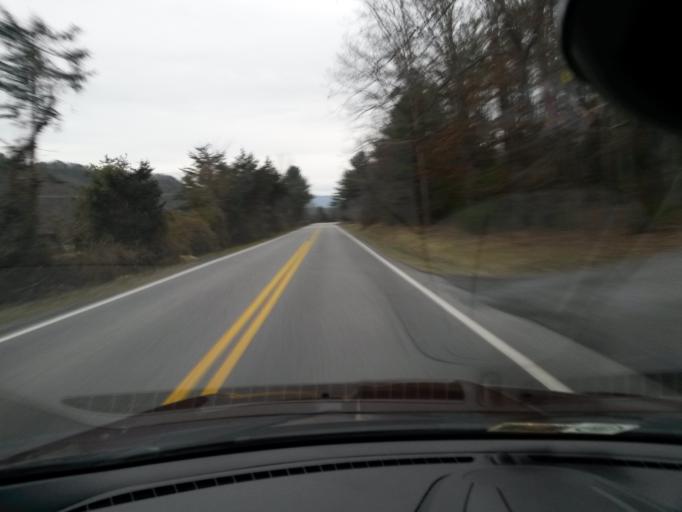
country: US
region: Virginia
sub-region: Bath County
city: Warm Springs
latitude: 38.0316
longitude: -79.6525
